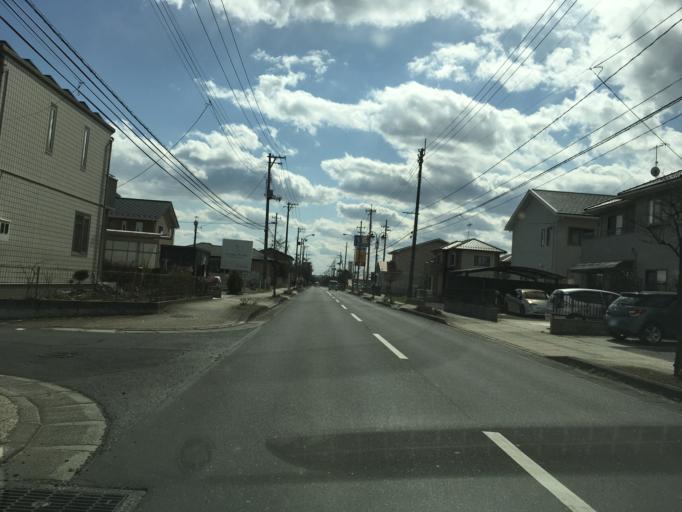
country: JP
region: Miyagi
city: Wakuya
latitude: 38.7020
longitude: 141.2123
